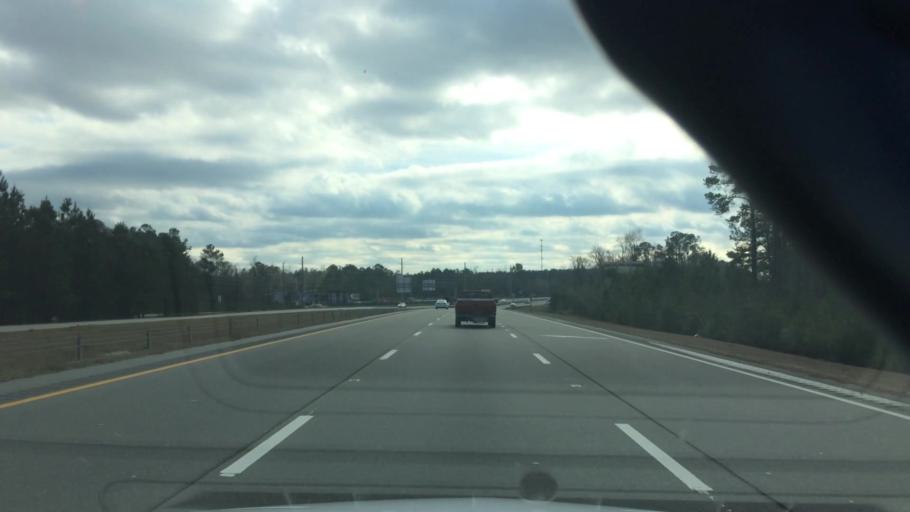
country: US
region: North Carolina
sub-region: Brunswick County
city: Leland
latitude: 34.1853
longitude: -78.0824
